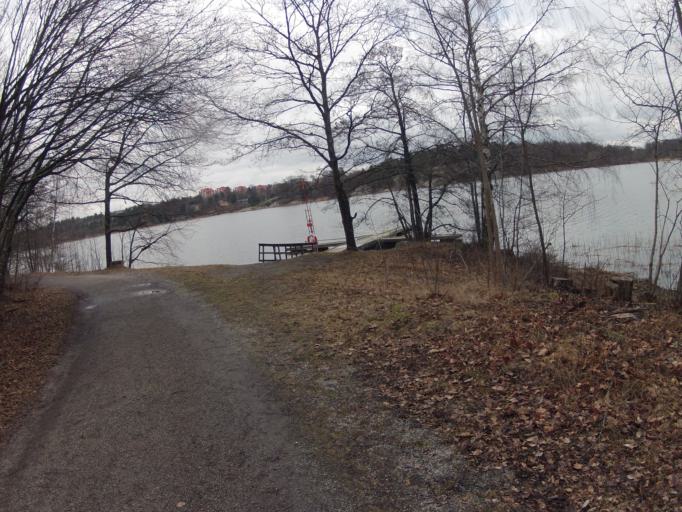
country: SE
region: Stockholm
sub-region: Norrtalje Kommun
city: Bergshamra
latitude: 59.3712
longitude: 18.0276
